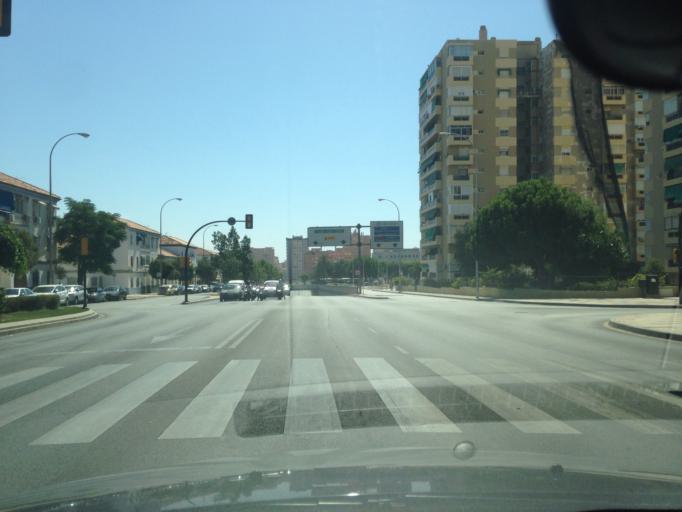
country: ES
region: Andalusia
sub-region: Provincia de Malaga
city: Malaga
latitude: 36.7175
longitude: -4.4487
